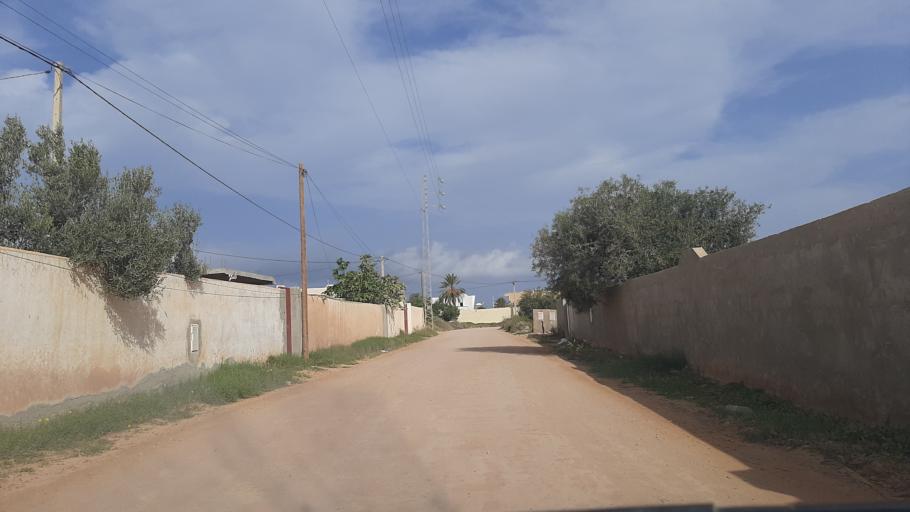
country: TN
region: Madanin
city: Midoun
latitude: 33.8144
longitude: 11.0251
